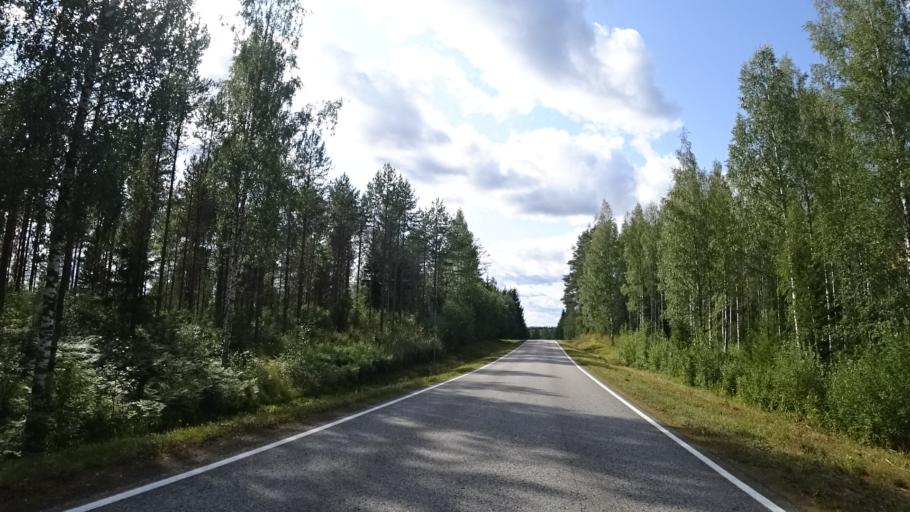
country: RU
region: Republic of Karelia
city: Vyartsilya
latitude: 62.2691
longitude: 30.7968
